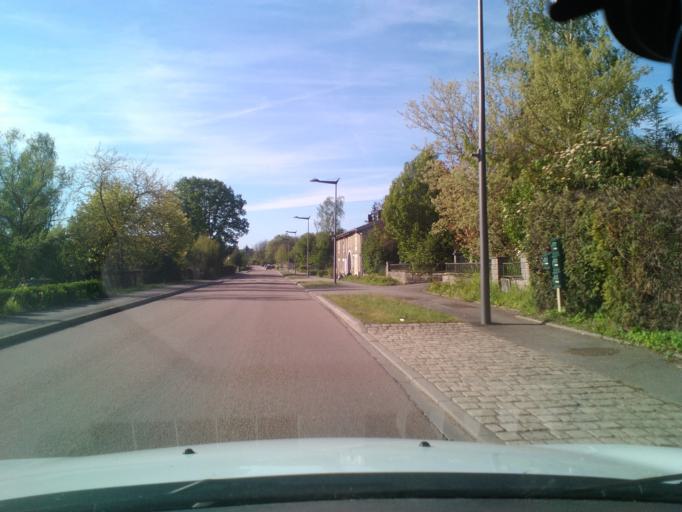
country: FR
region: Lorraine
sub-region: Departement des Vosges
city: Mirecourt
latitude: 48.3174
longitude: 6.1252
